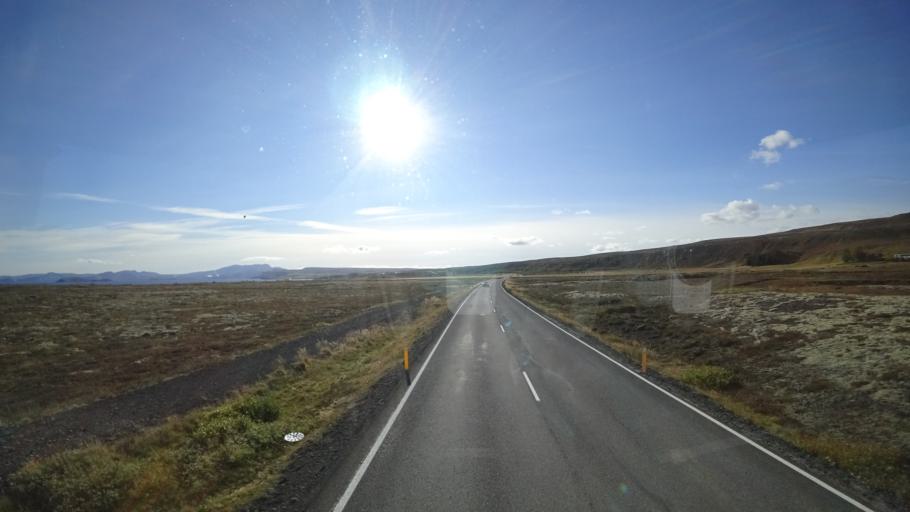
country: IS
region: South
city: Hveragerdi
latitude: 64.2475
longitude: -21.1653
